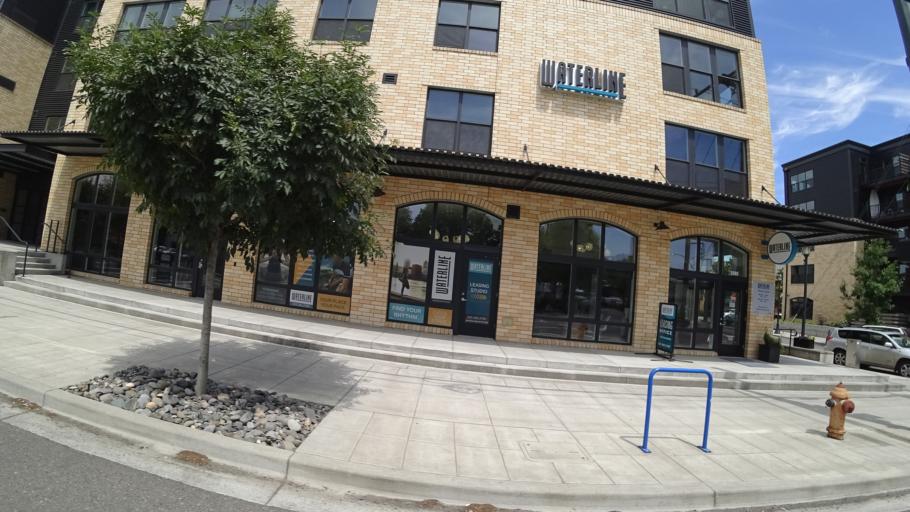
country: US
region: Oregon
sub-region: Multnomah County
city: Portland
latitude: 45.5383
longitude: -122.6885
